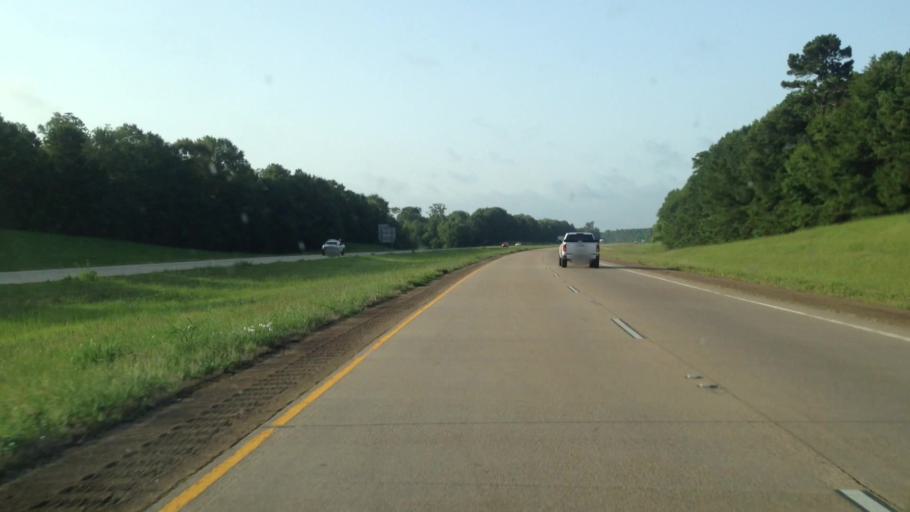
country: US
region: Louisiana
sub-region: Rapides Parish
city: Woodworth
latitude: 31.1545
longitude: -92.4546
